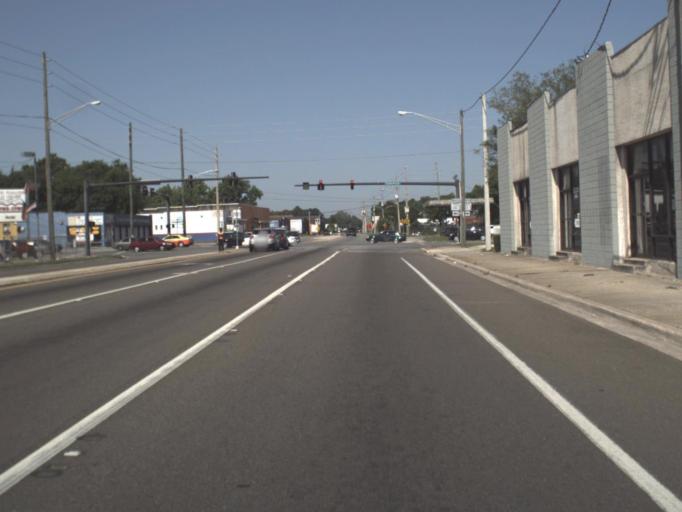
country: US
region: Florida
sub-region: Duval County
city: Jacksonville
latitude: 30.3278
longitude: -81.7298
